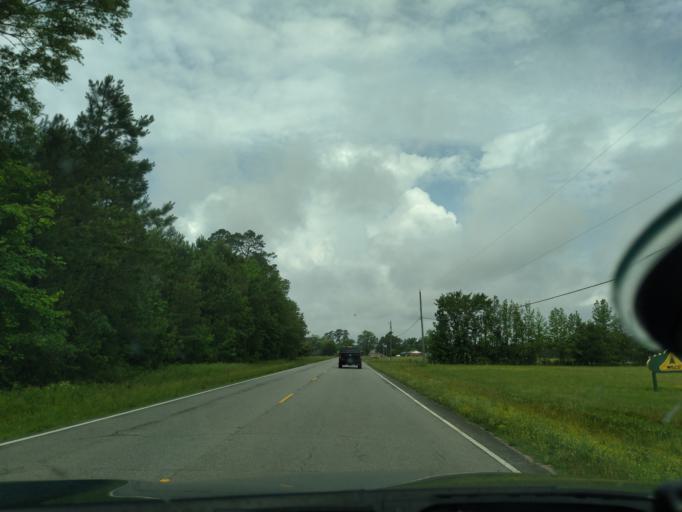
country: US
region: North Carolina
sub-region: Washington County
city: Plymouth
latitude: 35.8752
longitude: -76.6328
